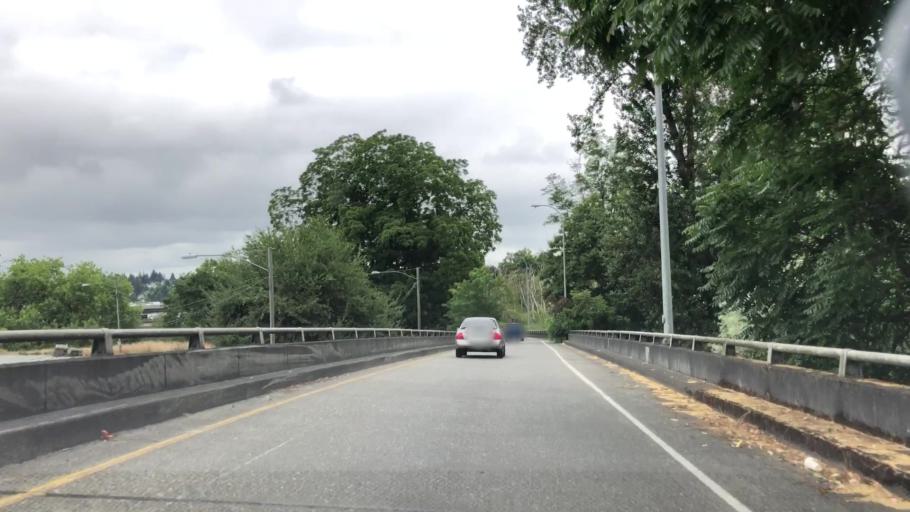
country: US
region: Washington
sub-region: King County
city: Seattle
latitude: 47.6428
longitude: -122.2960
